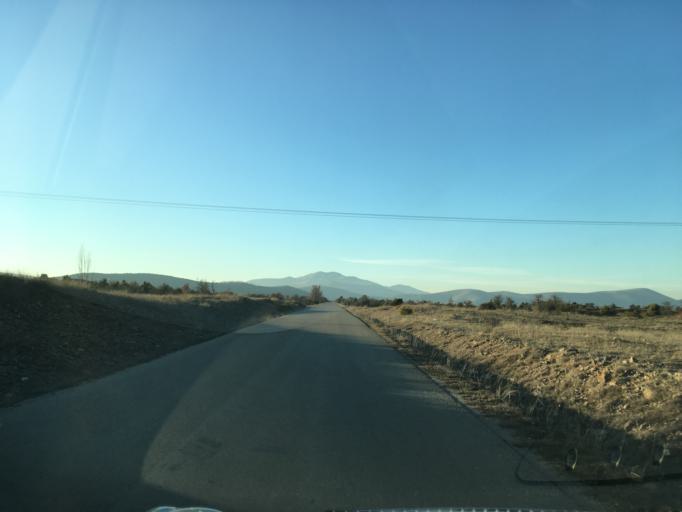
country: GR
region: West Macedonia
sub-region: Nomos Kozanis
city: Kozani
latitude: 40.2722
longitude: 21.7381
